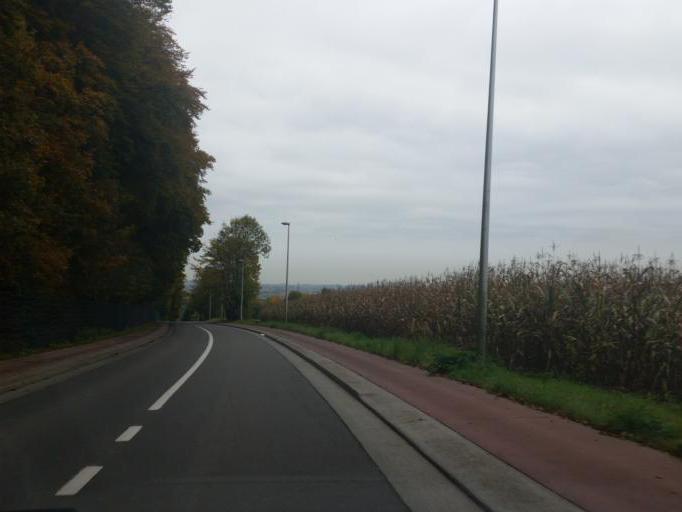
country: BE
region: Flanders
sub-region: Provincie Vlaams-Brabant
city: Beersel
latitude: 50.7434
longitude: 4.2936
